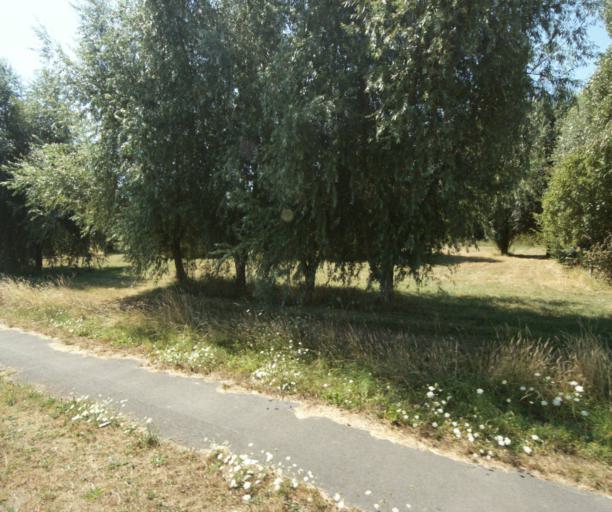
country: FR
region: Nord-Pas-de-Calais
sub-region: Departement du Nord
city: Halluin
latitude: 50.7736
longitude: 3.1116
